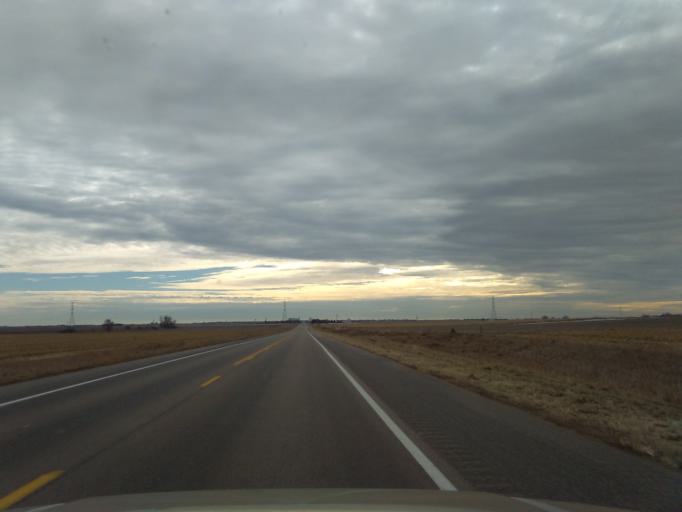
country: US
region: Nebraska
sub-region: Kearney County
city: Minden
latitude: 40.5584
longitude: -98.9518
